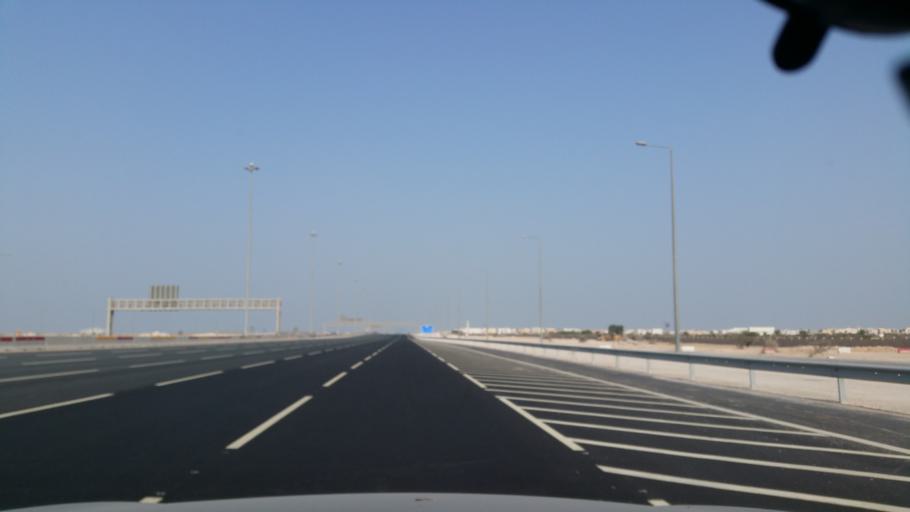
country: QA
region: Baladiyat Umm Salal
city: Umm Salal `Ali
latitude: 25.4509
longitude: 51.4208
